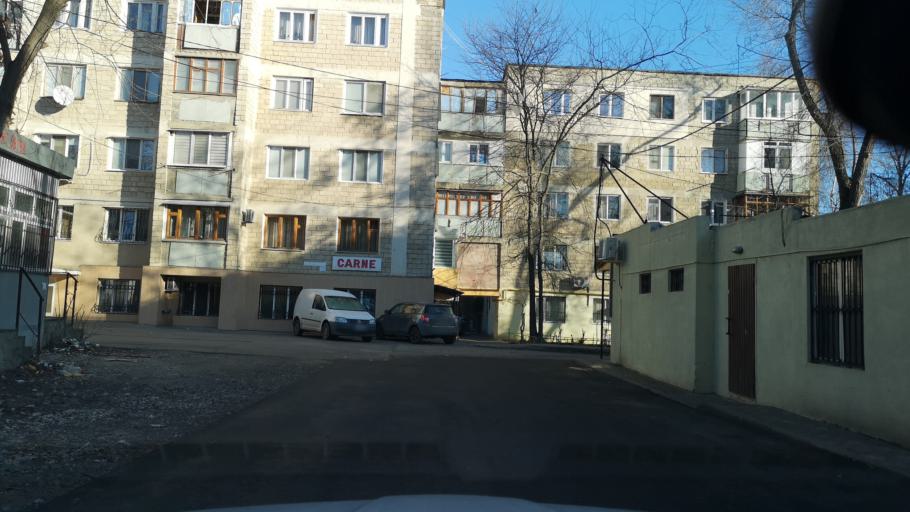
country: MD
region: Chisinau
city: Chisinau
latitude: 47.0344
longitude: 28.8809
